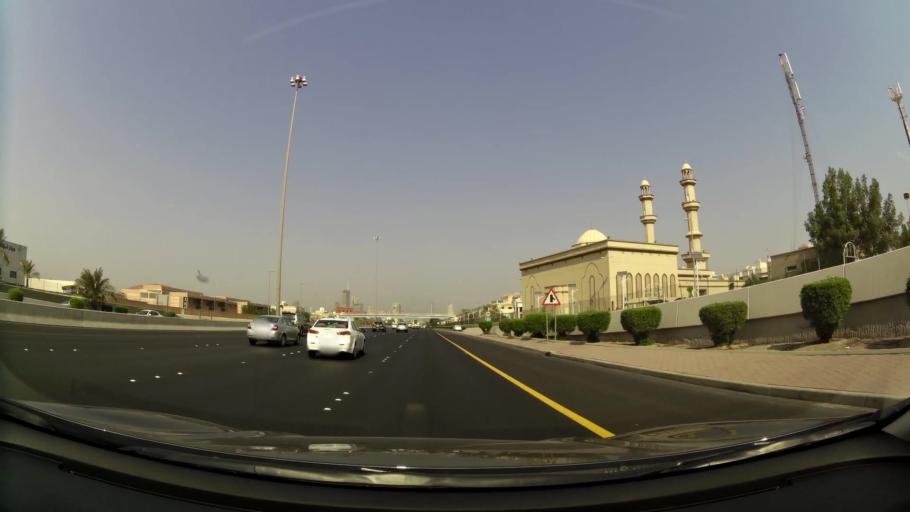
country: KW
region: Al Asimah
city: Ad Dasmah
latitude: 29.3418
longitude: 47.9999
